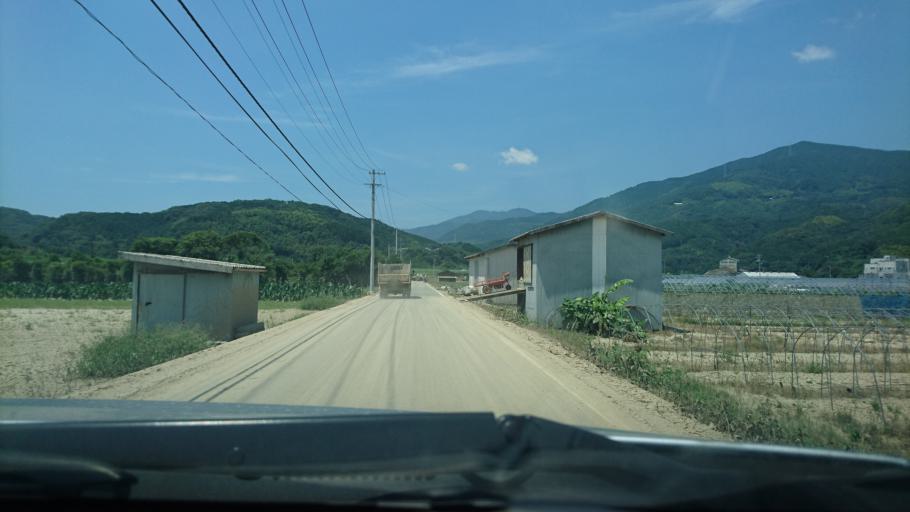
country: JP
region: Ehime
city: Ozu
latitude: 33.5336
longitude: 132.5674
